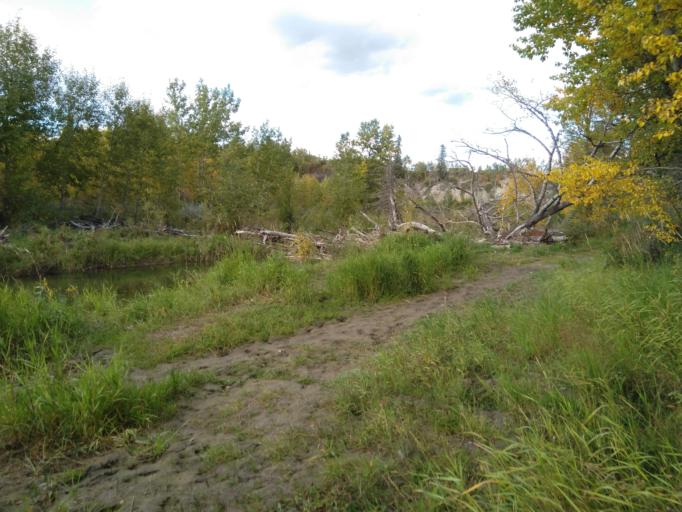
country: CA
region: Alberta
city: Cochrane
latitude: 51.1886
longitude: -114.4989
